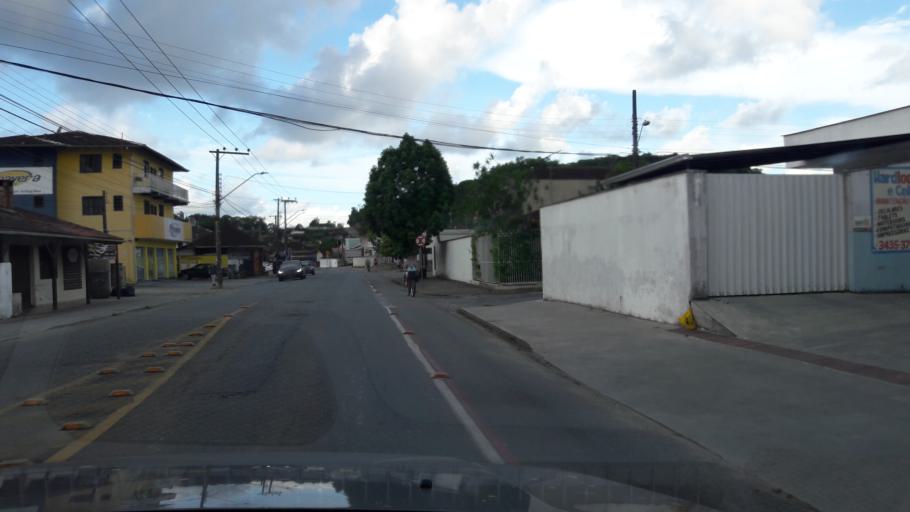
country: BR
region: Santa Catarina
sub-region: Joinville
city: Joinville
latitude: -26.3256
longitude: -48.8302
